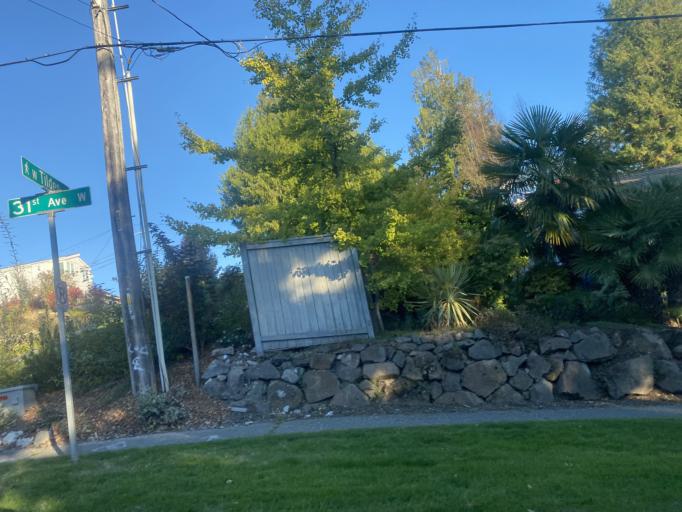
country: US
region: Washington
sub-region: King County
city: Seattle
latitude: 47.6531
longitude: -122.3969
